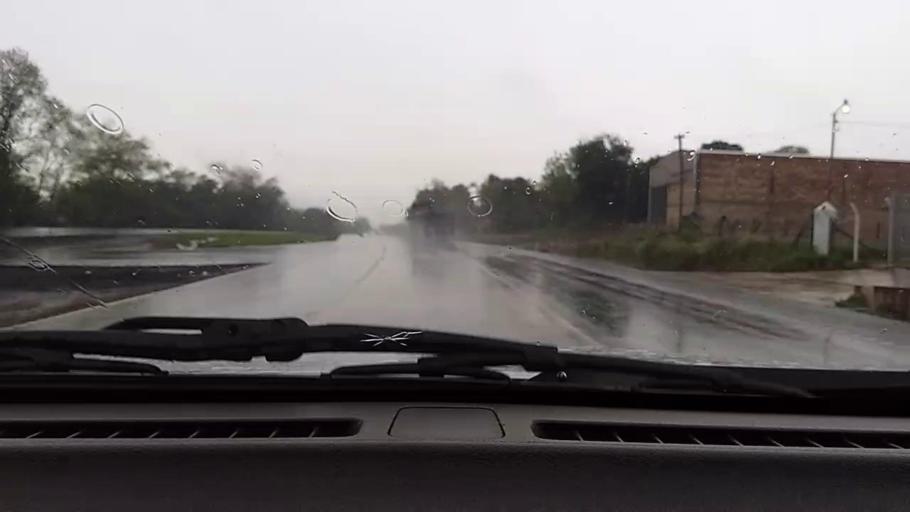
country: PY
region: Caaguazu
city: Repatriacion
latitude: -25.4463
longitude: -55.8878
